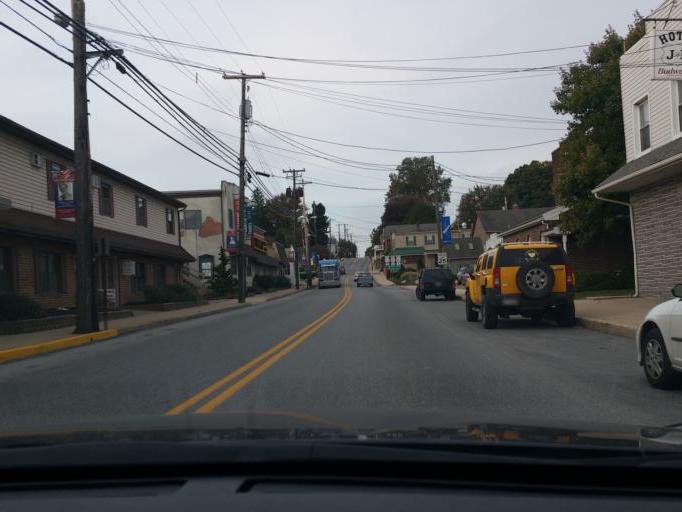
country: US
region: Pennsylvania
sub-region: Lancaster County
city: Quarryville
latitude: 39.8978
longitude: -76.1618
